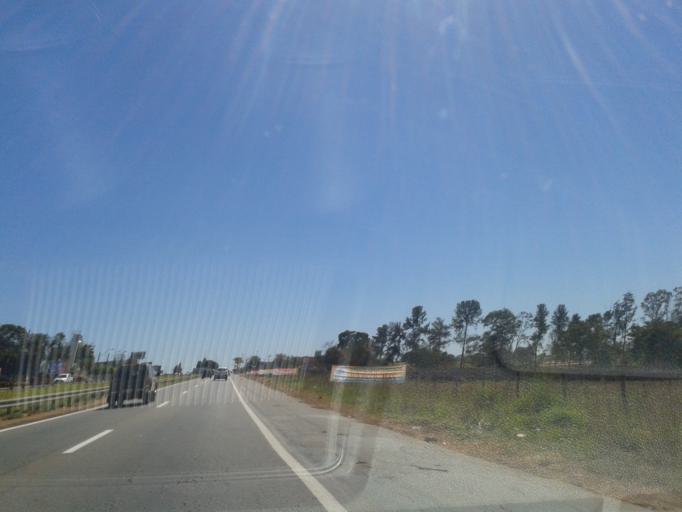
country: BR
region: Goias
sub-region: Goiania
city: Goiania
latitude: -16.6242
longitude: -49.3539
